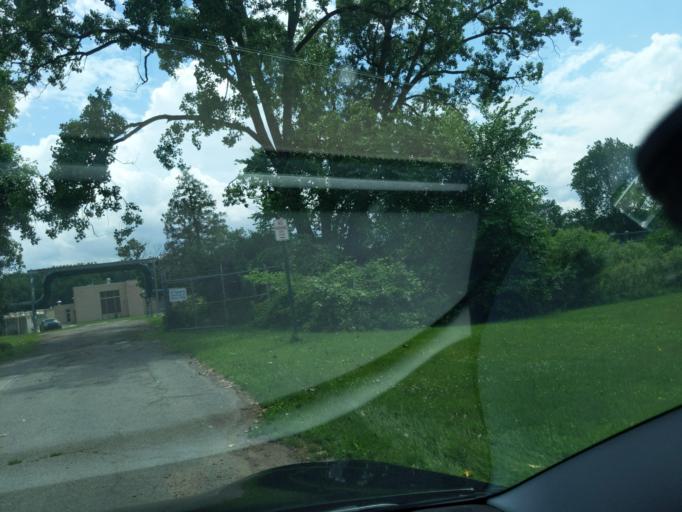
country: US
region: Michigan
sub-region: Jackson County
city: Jackson
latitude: 42.2834
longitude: -84.4104
